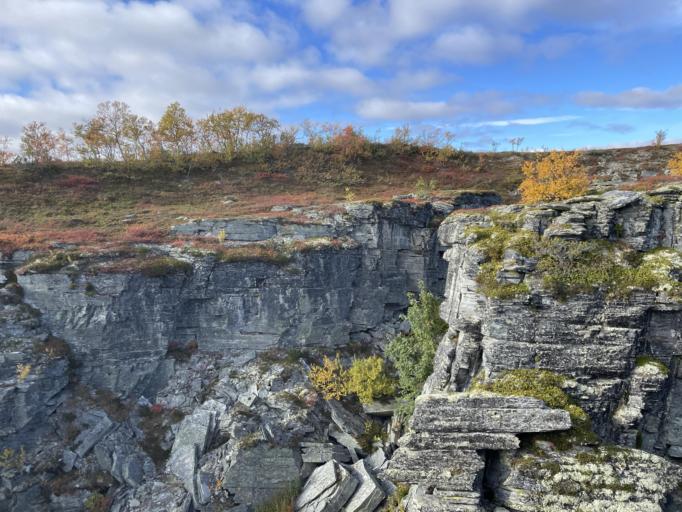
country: SE
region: Jaemtland
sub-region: Are Kommun
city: Are
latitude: 62.6922
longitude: 12.9095
